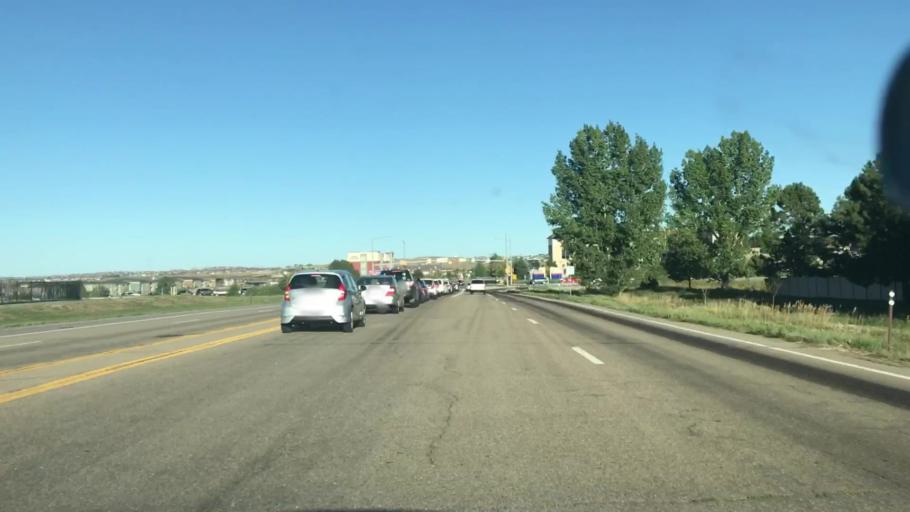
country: US
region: Colorado
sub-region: Boulder County
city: Lafayette
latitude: 39.9724
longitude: -105.0926
